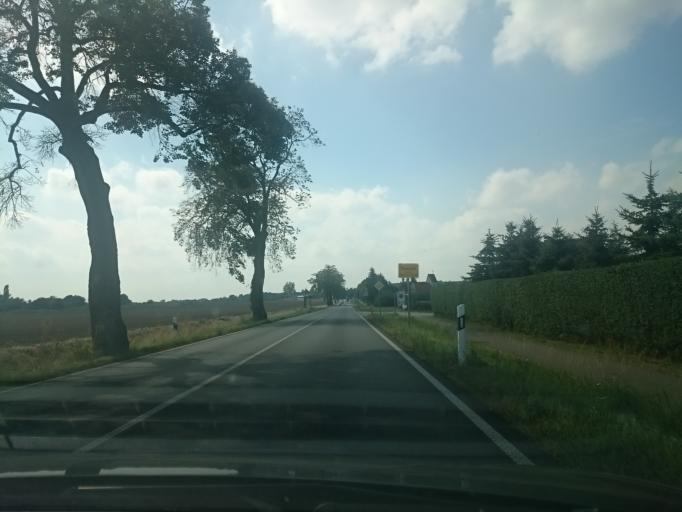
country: DE
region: Mecklenburg-Vorpommern
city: Pasewalk
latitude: 53.5053
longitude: 14.0216
